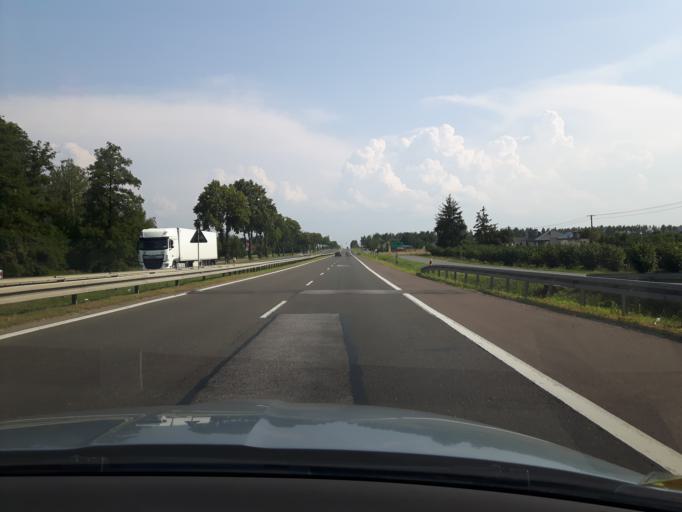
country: PL
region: Masovian Voivodeship
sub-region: Powiat plonski
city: Zaluski
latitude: 52.5654
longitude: 20.4889
